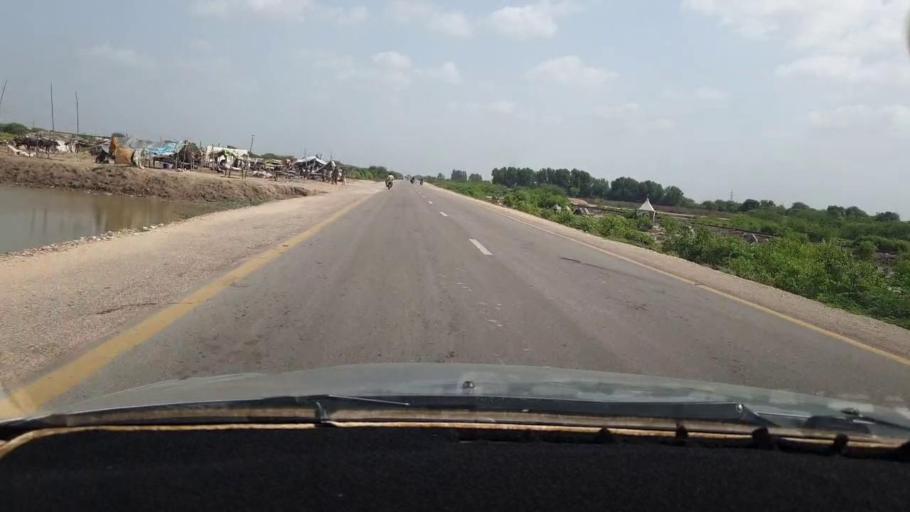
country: PK
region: Sindh
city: Digri
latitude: 25.1144
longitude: 69.1574
